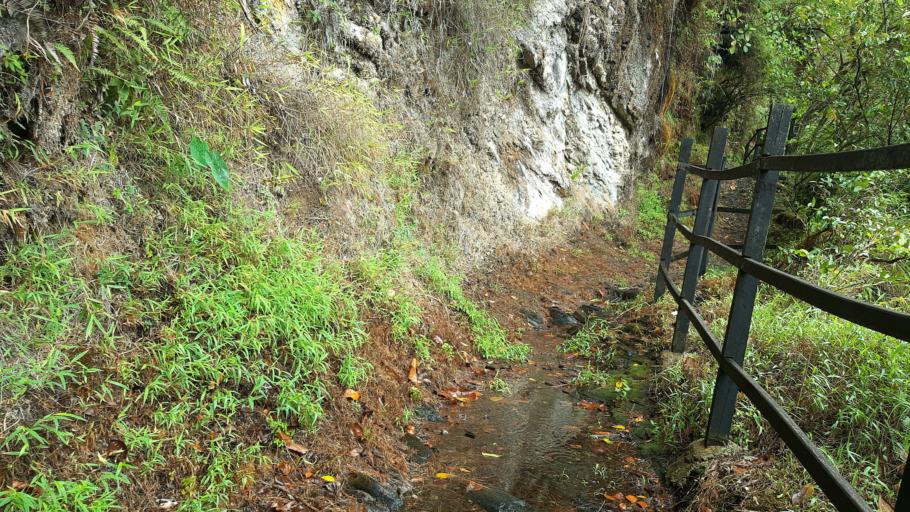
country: CO
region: Boyaca
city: Santa Maria
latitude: 4.9111
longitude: -73.2985
